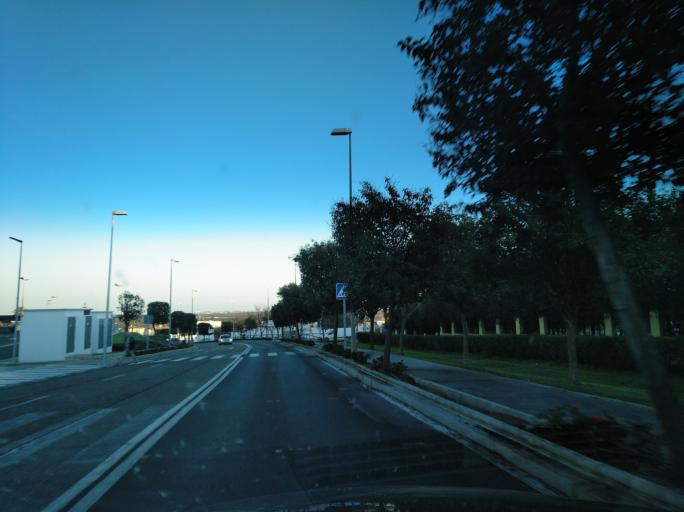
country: ES
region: Andalusia
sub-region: Provincia de Huelva
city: Ayamonte
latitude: 37.2199
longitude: -7.3978
